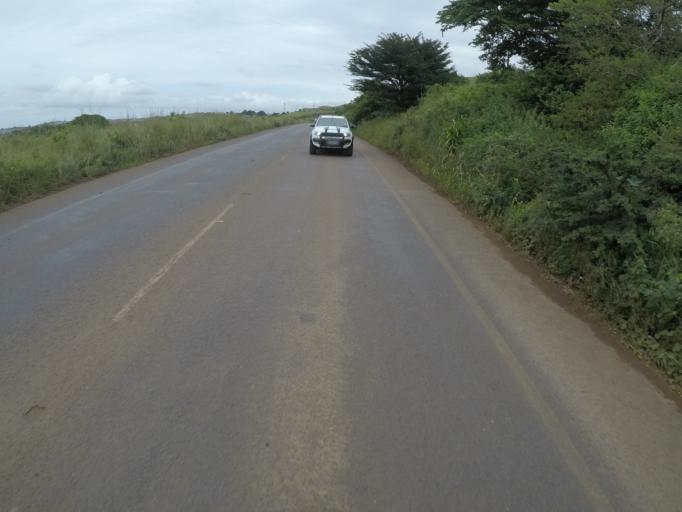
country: ZA
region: KwaZulu-Natal
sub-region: uThungulu District Municipality
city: Empangeni
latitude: -28.7530
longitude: 31.8762
